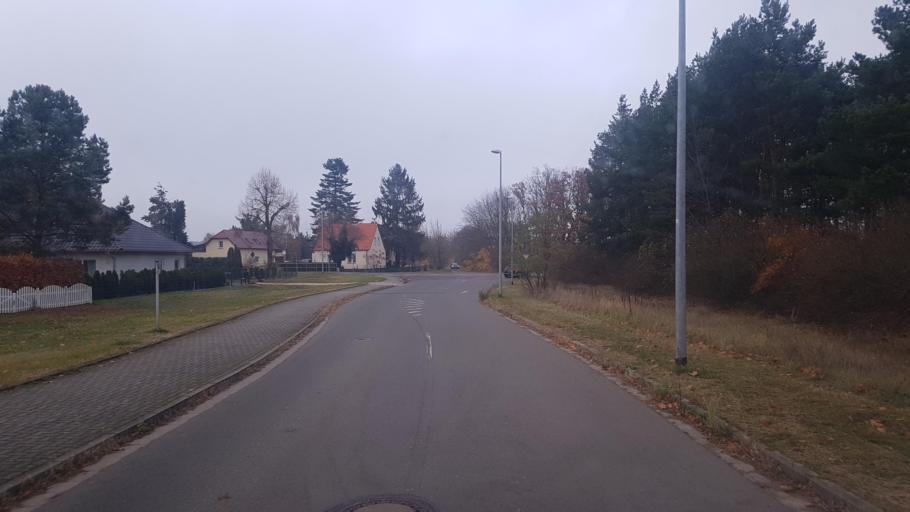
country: DE
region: Brandenburg
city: Gross Kreutz
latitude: 52.4067
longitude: 12.7334
